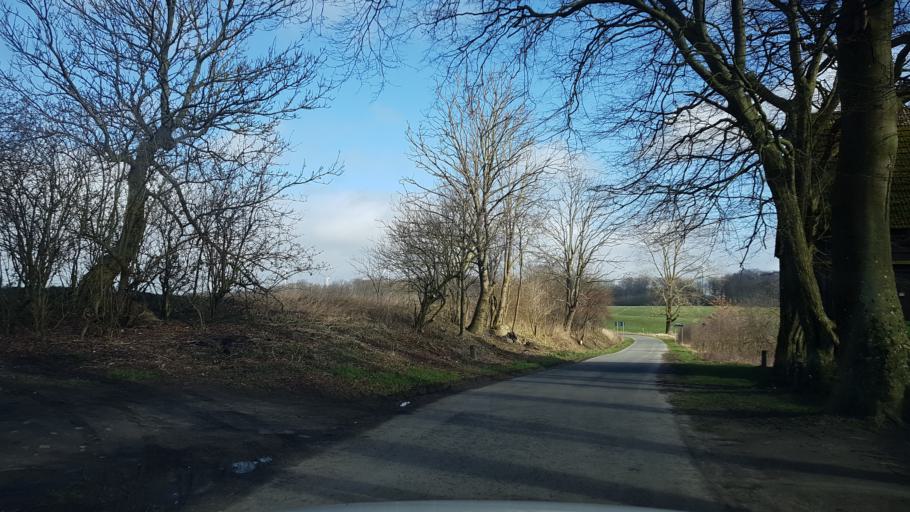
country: PL
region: West Pomeranian Voivodeship
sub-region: Powiat slawienski
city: Slawno
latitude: 54.4812
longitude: 16.6512
